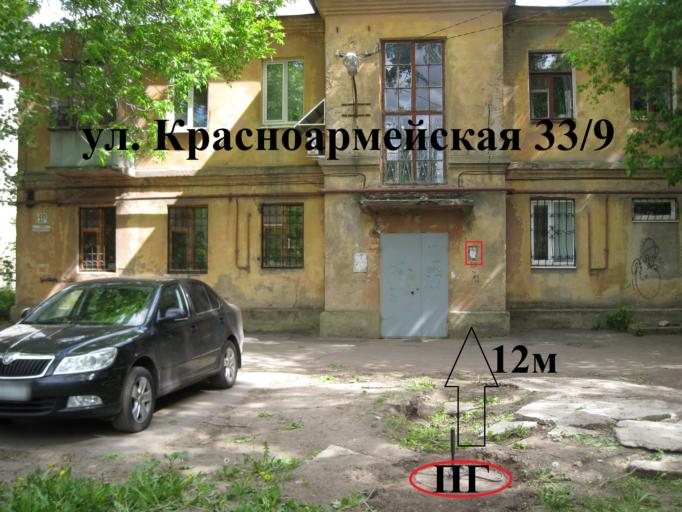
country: RU
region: Voronezj
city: Voronezh
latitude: 51.6591
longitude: 39.1817
